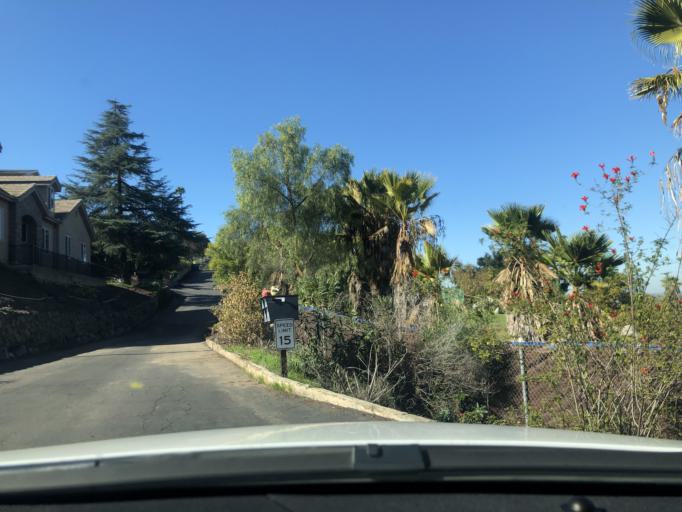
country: US
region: California
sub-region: San Diego County
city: Bostonia
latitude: 32.7845
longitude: -116.9407
